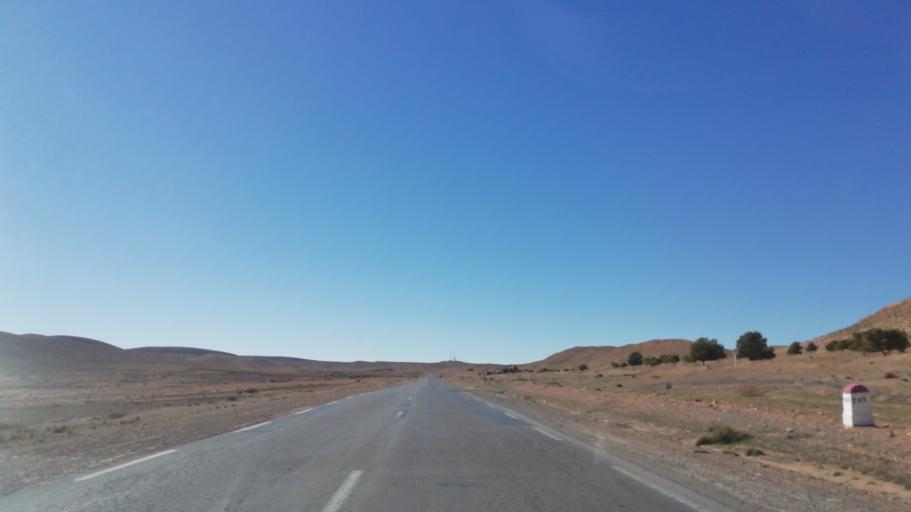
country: DZ
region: El Bayadh
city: El Bayadh
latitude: 33.6758
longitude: 1.4473
